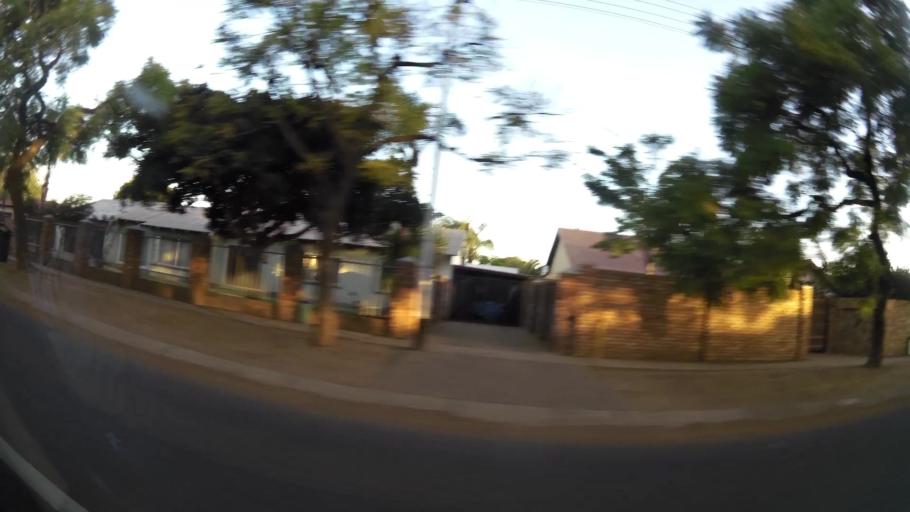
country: ZA
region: Gauteng
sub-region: City of Tshwane Metropolitan Municipality
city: Pretoria
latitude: -25.7115
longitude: 28.2381
